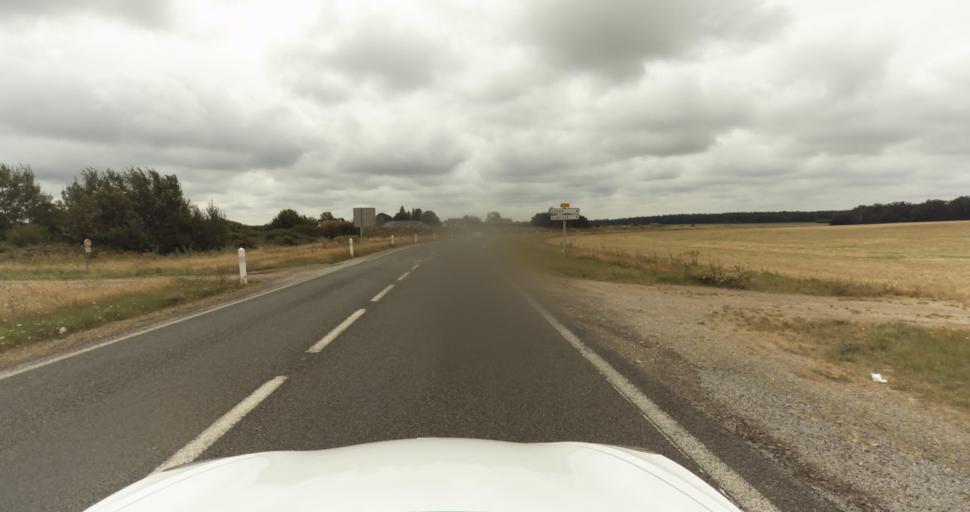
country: FR
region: Haute-Normandie
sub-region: Departement de l'Eure
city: Saint-Sebastien-de-Morsent
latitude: 49.0358
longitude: 1.0892
